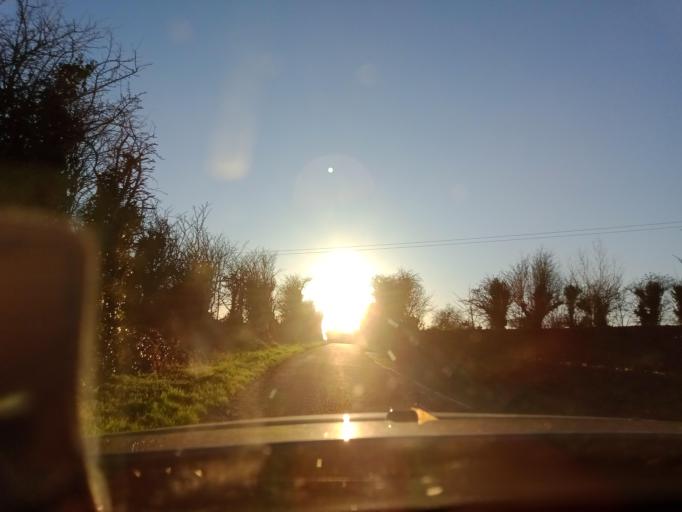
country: IE
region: Leinster
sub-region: Loch Garman
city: New Ross
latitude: 52.3798
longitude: -7.0092
